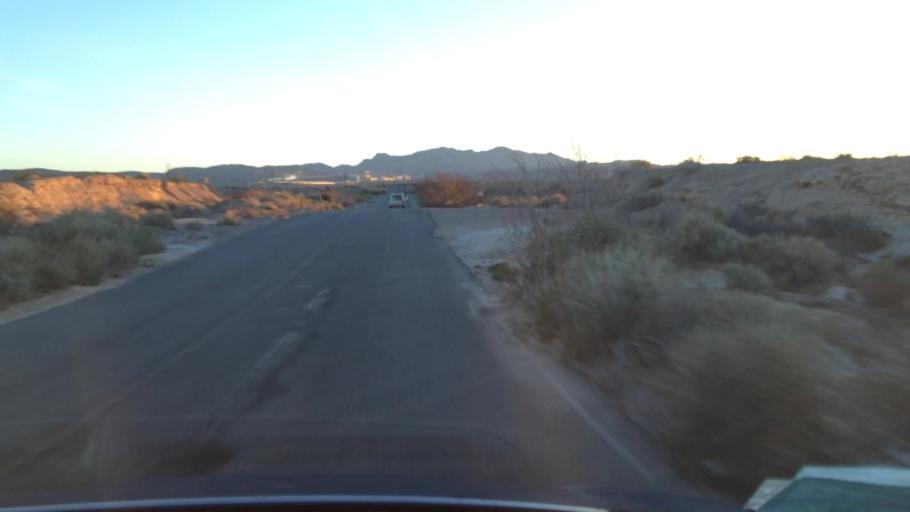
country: US
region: Nevada
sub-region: Clark County
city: Nellis Air Force Base
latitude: 36.2160
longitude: -114.8958
